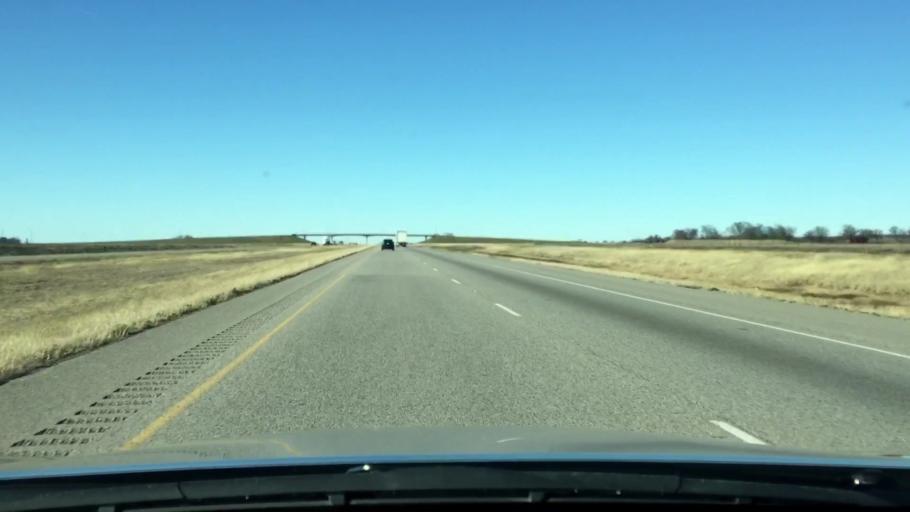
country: US
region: Texas
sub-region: Hill County
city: Itasca
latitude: 32.1210
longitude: -97.1163
